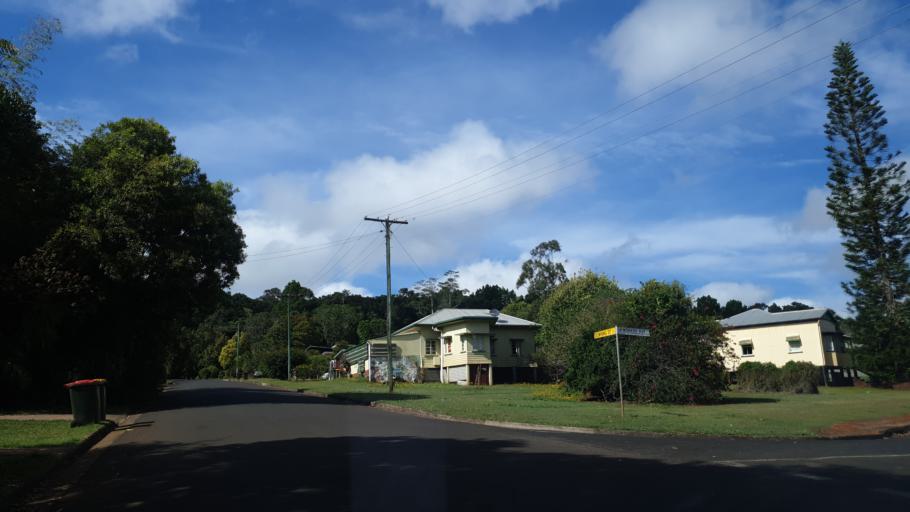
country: AU
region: Queensland
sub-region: Tablelands
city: Atherton
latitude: -17.3530
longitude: 145.5912
